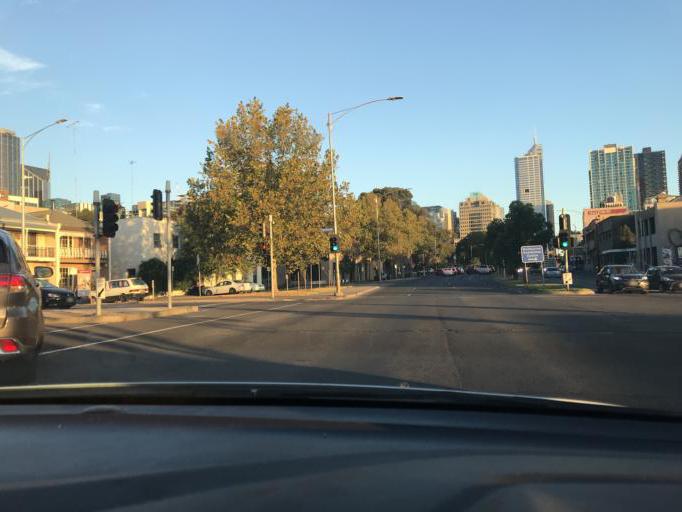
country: AU
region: Victoria
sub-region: Melbourne
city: West Melbourne
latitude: -37.8078
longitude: 144.9515
